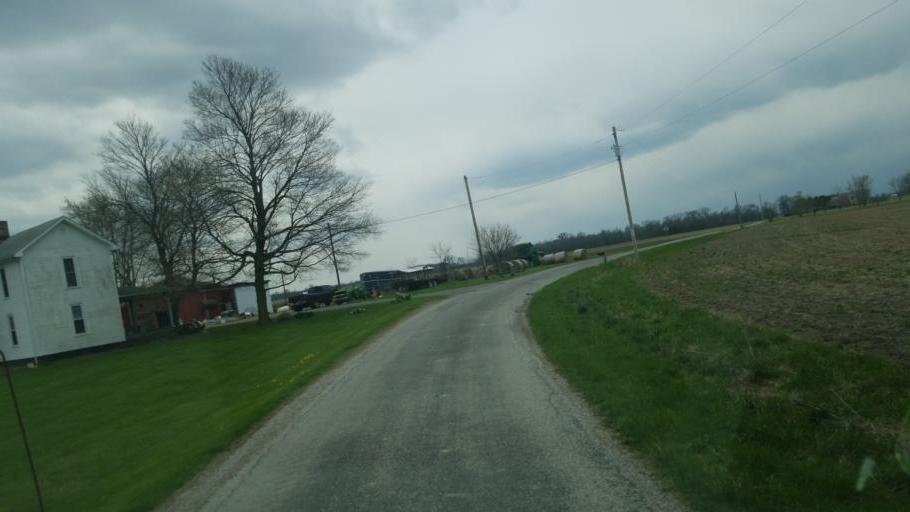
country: US
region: Ohio
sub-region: Marion County
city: Prospect
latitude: 40.3858
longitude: -83.2233
